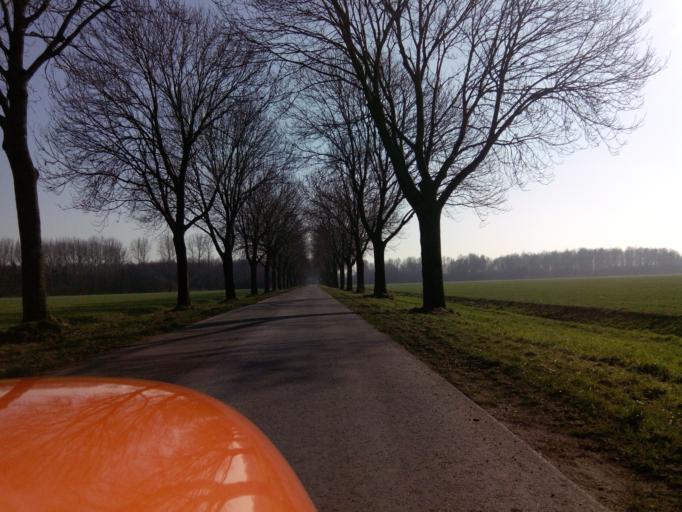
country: NL
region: Gelderland
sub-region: Gemeente Nijkerk
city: Nijkerk
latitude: 52.2724
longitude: 5.4800
